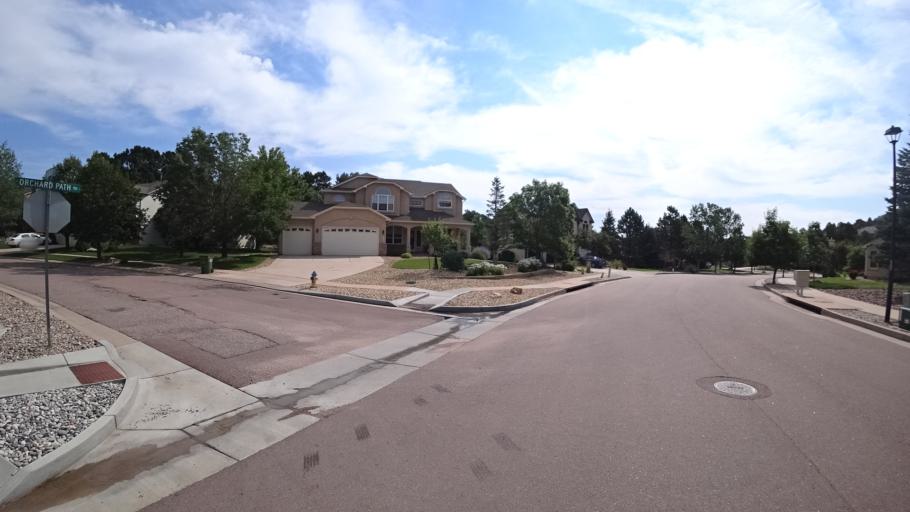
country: US
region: Colorado
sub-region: El Paso County
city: Air Force Academy
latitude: 38.9429
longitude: -104.8660
